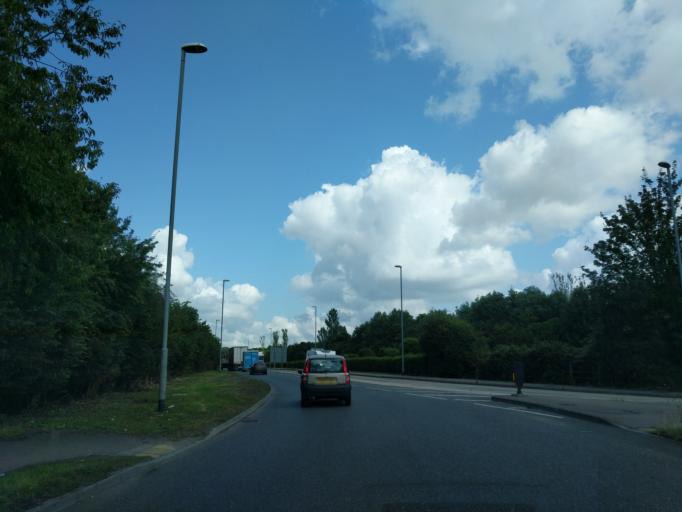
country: GB
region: England
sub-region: Suffolk
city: Exning
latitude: 52.2912
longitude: 0.3911
